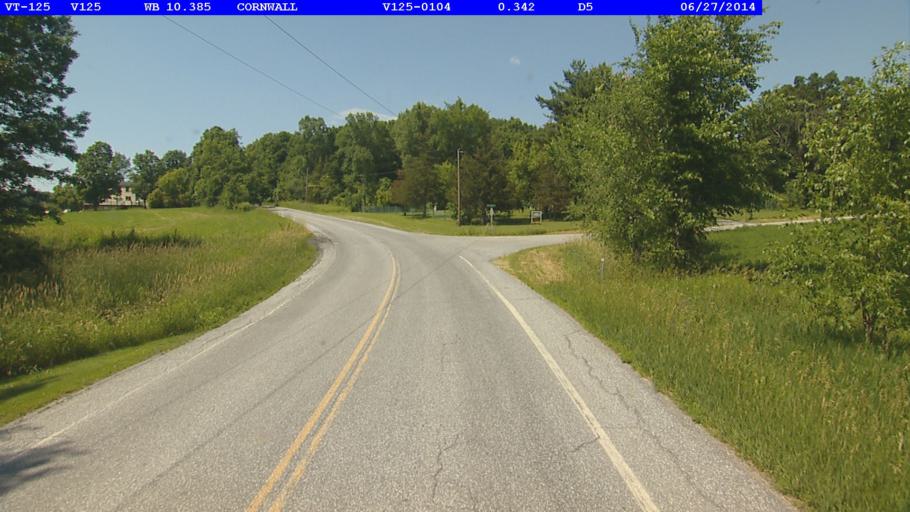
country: US
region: Vermont
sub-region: Addison County
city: Middlebury (village)
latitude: 43.9932
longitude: -73.2526
